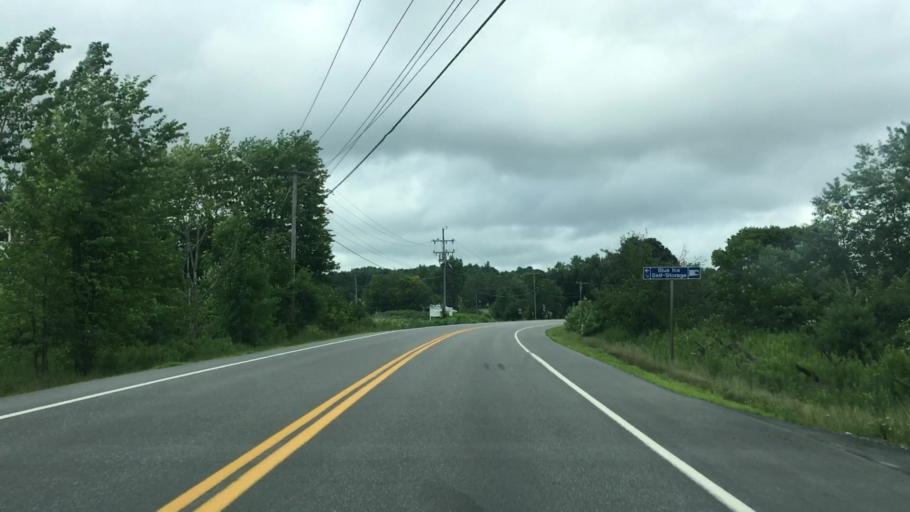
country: US
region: Maine
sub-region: Kennebec County
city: Pittston
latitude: 44.1982
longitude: -69.7526
